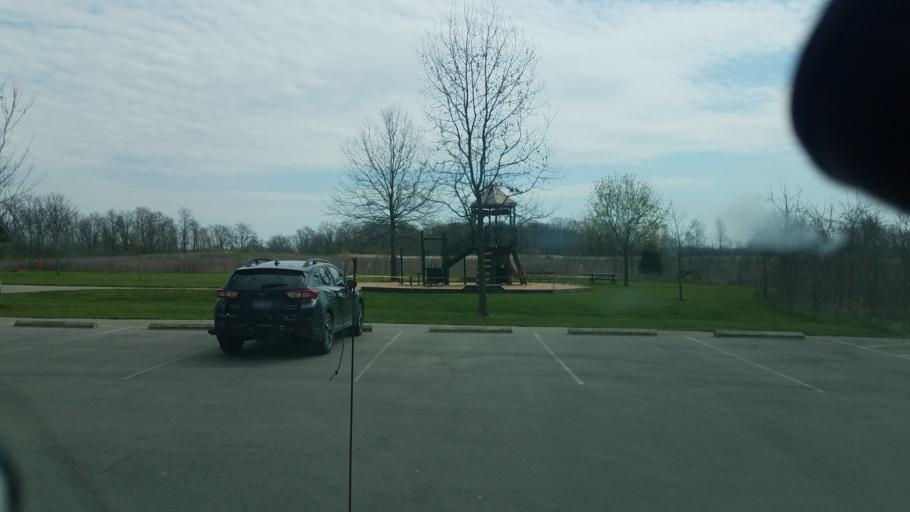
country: US
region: Ohio
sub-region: Delaware County
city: Delaware
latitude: 40.3448
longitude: -83.1170
